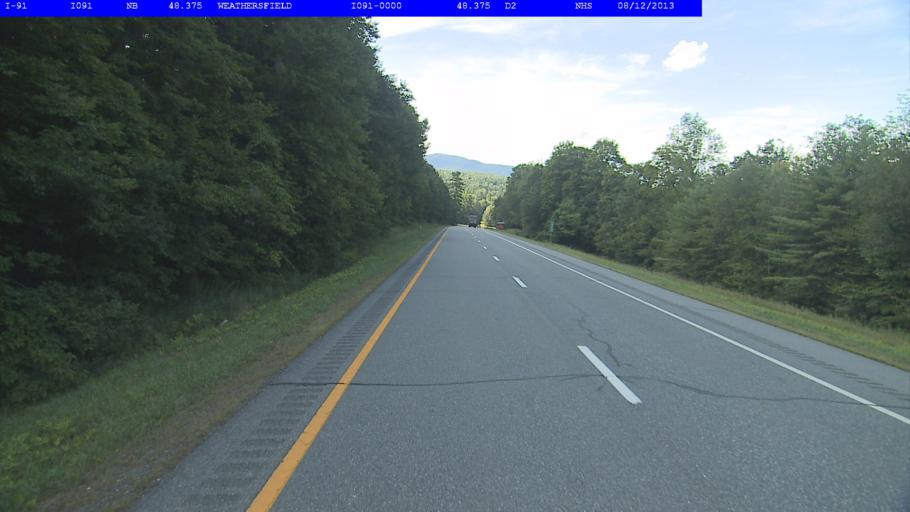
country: US
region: New Hampshire
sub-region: Sullivan County
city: Claremont
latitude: 43.3606
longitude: -72.4239
